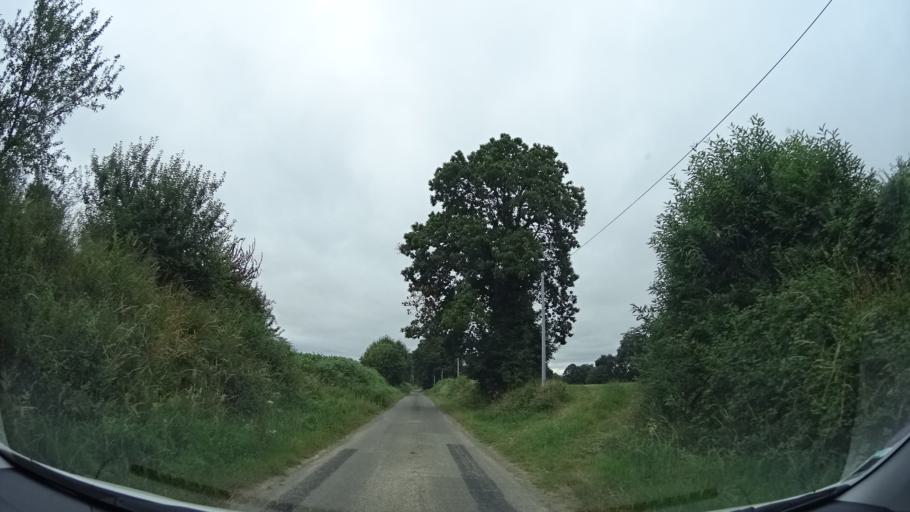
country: FR
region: Brittany
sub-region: Departement des Cotes-d'Armor
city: Evran
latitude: 48.3339
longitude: -1.9488
